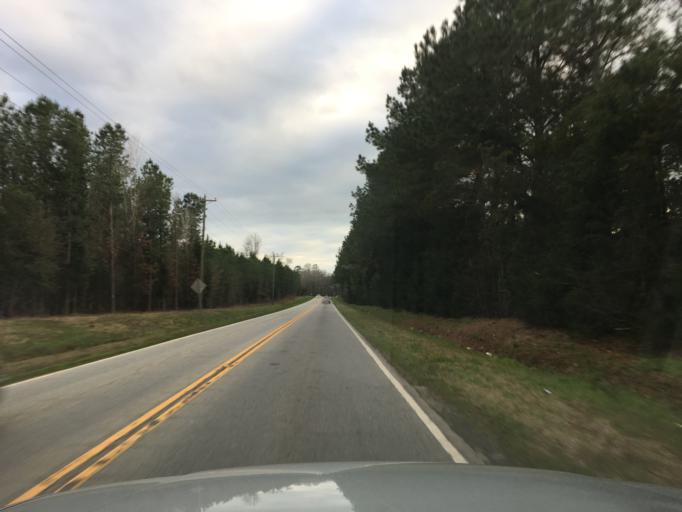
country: US
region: South Carolina
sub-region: Saluda County
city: Saluda
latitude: 33.9815
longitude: -81.7701
